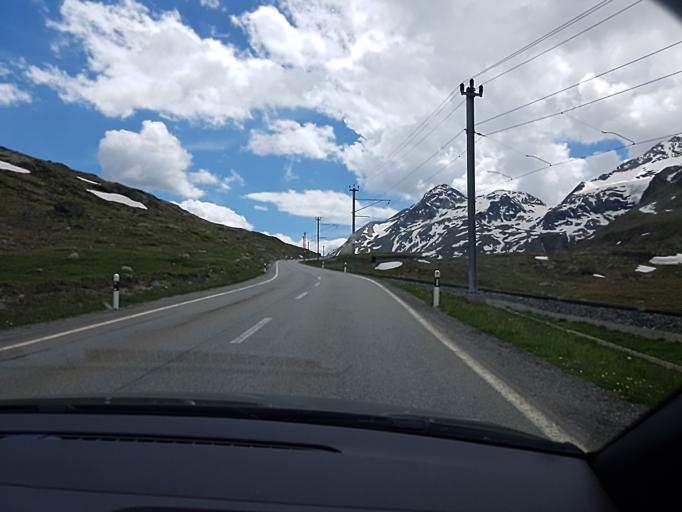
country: CH
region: Grisons
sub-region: Bernina District
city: Poschiavo
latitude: 46.4245
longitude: 10.0006
